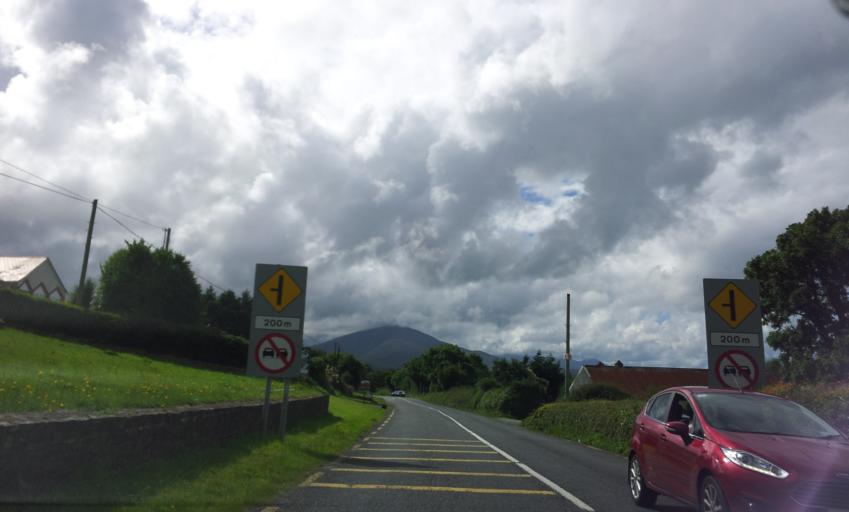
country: IE
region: Munster
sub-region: Ciarrai
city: Killorglin
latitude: 52.2260
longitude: -9.8956
